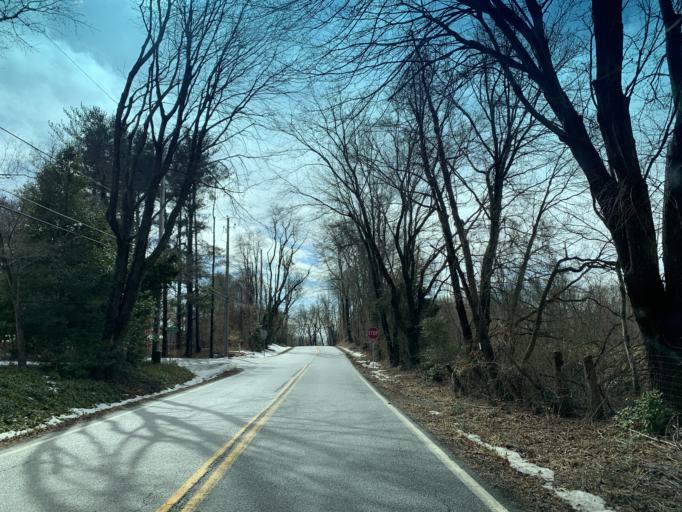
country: US
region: Delaware
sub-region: New Castle County
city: Newark
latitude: 39.7153
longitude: -75.7993
